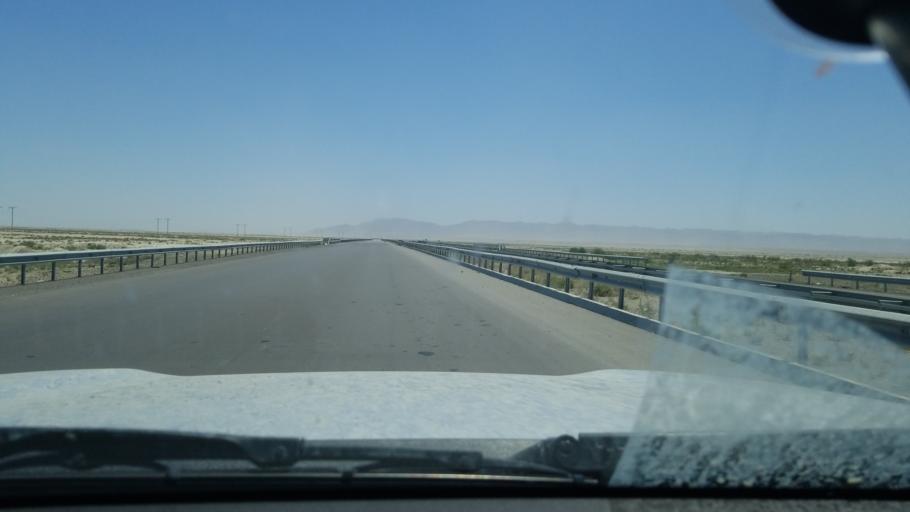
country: TM
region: Balkan
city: Gazanjyk
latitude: 39.2751
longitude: 55.2670
